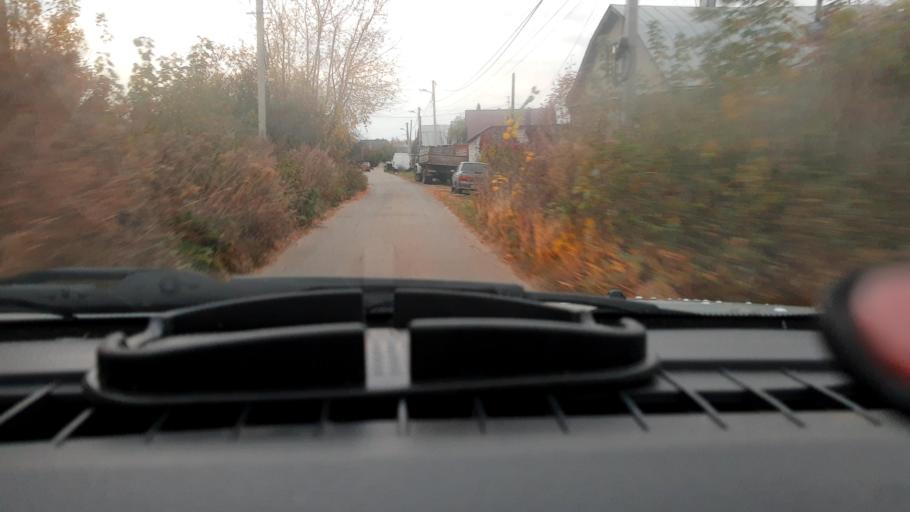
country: RU
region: Nizjnij Novgorod
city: Nizhniy Novgorod
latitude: 56.2545
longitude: 43.9928
